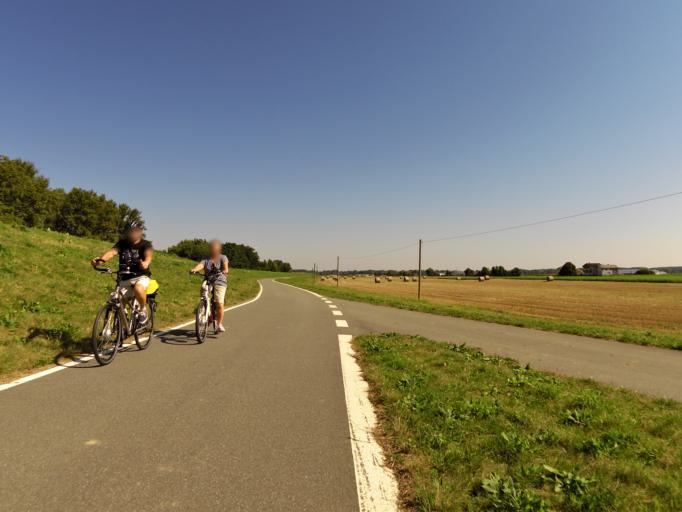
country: DE
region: Rheinland-Pfalz
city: Nackenheim
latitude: 49.9062
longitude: 8.3610
